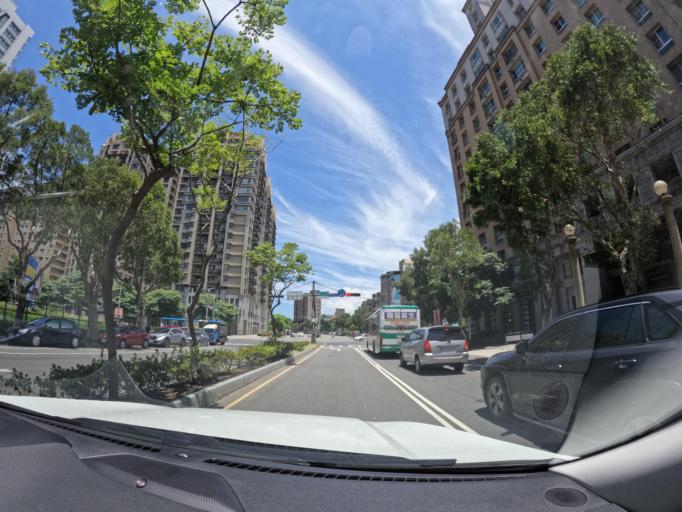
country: TW
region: Taiwan
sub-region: Taoyuan
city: Taoyuan
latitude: 25.0821
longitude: 121.3794
